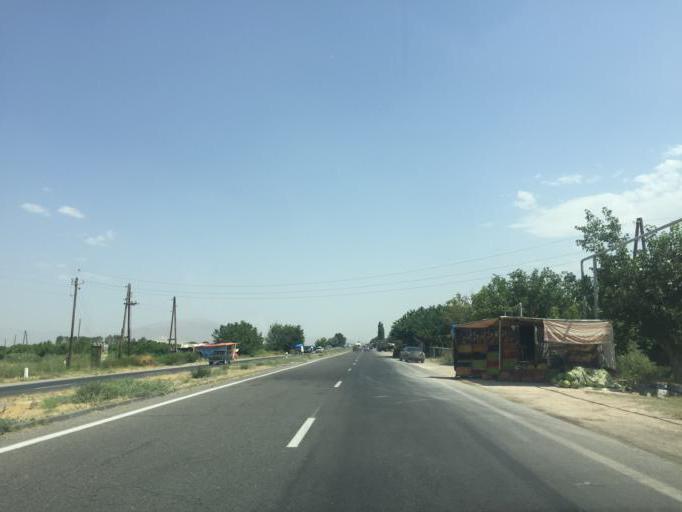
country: AM
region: Ararat
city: Shahumyan
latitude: 39.9102
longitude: 44.6020
